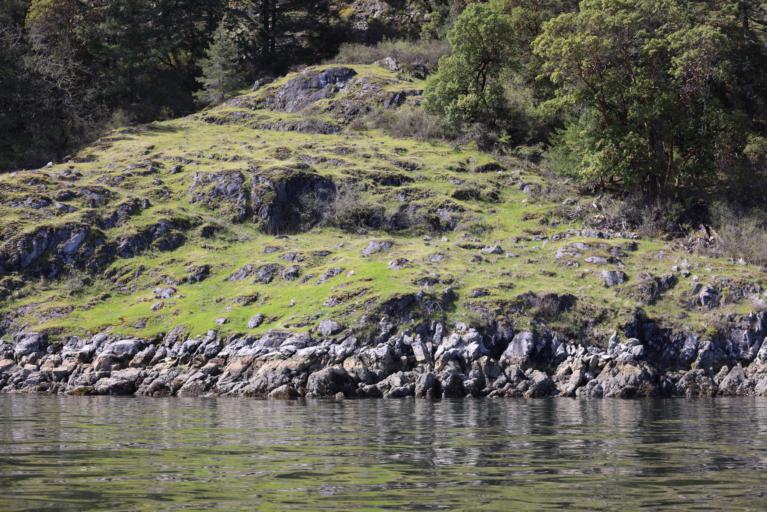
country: CA
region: British Columbia
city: Langford
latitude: 48.5800
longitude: -123.5190
